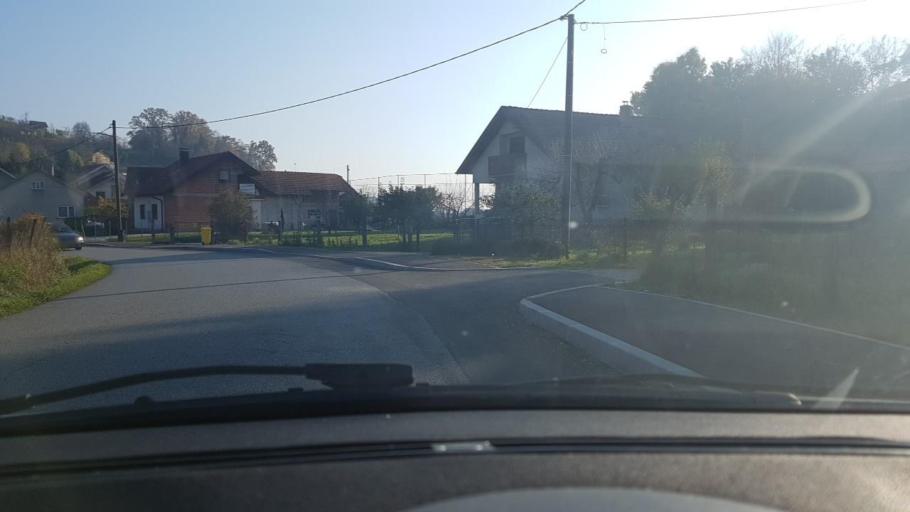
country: HR
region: Krapinsko-Zagorska
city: Zabok
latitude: 46.0235
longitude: 15.8861
